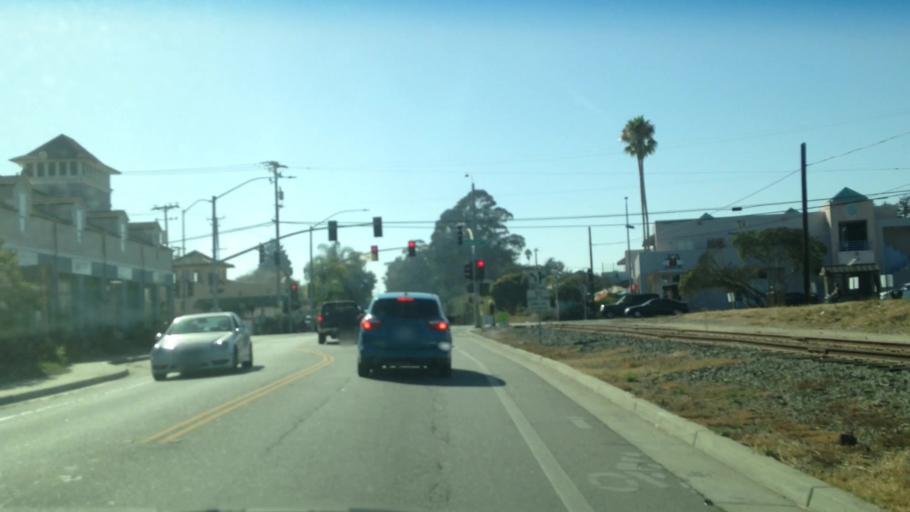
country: US
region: California
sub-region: Santa Cruz County
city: Twin Lakes
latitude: 36.9675
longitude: -122.0071
